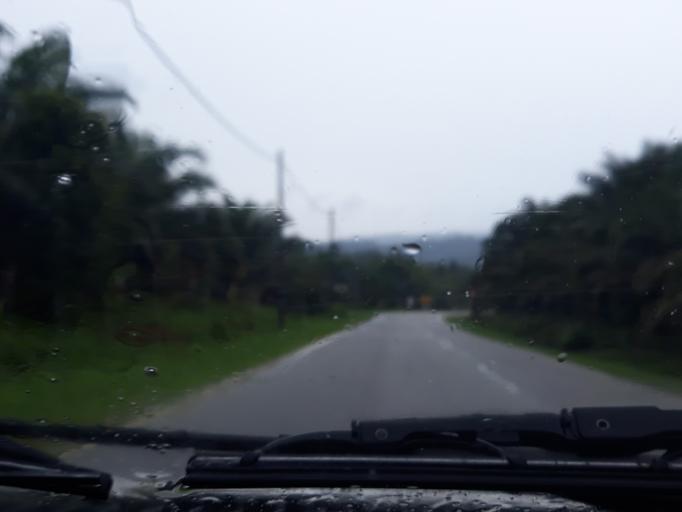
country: MY
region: Kedah
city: Kulim
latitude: 5.2828
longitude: 100.6236
